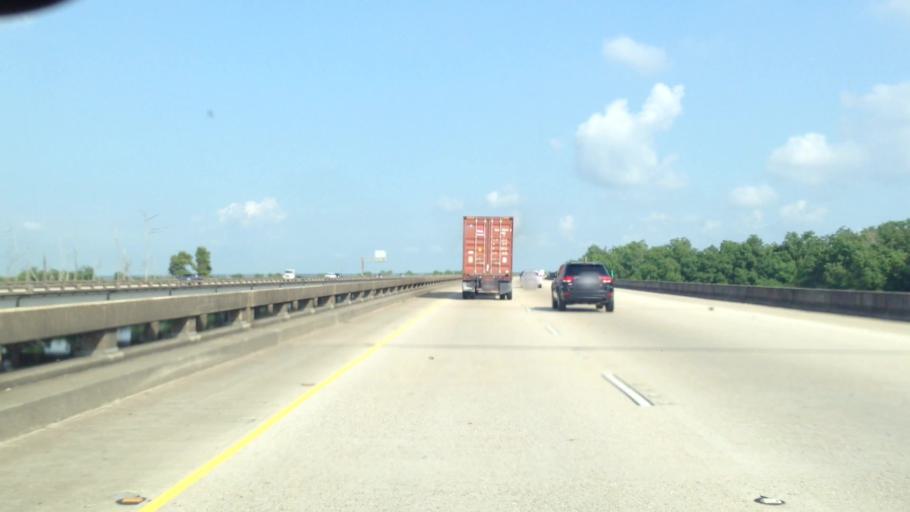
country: US
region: Louisiana
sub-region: Saint Charles Parish
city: Ama
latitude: 30.0096
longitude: -90.3023
